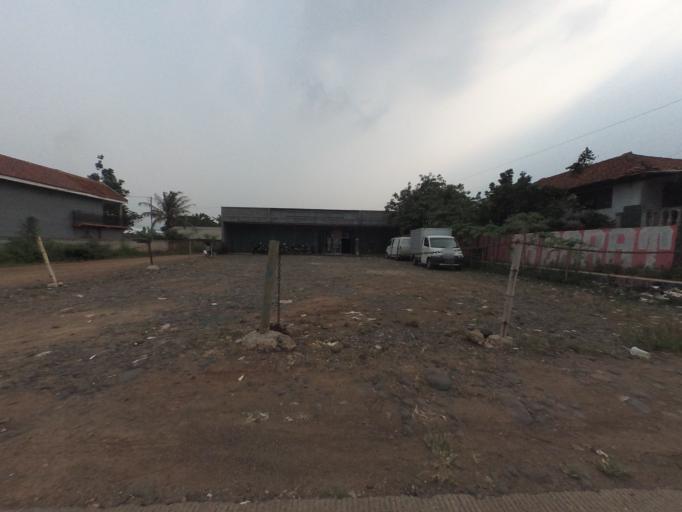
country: ID
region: West Java
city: Sidoger Lebak
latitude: -6.5650
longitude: 106.5872
